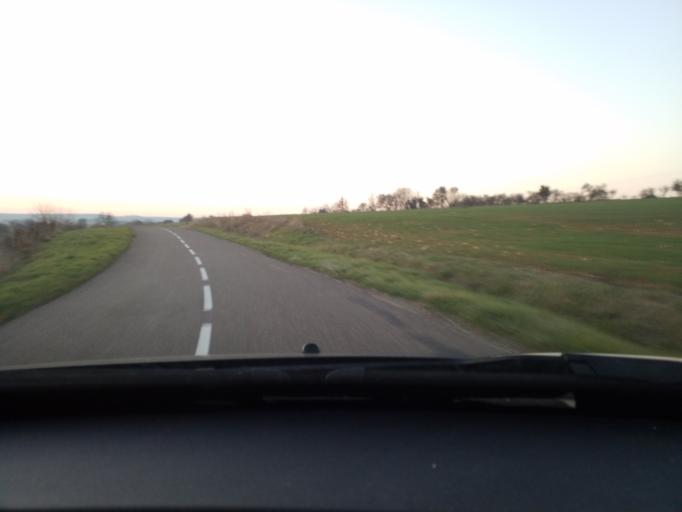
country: FR
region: Franche-Comte
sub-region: Departement de la Haute-Saone
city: Faverney
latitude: 47.8824
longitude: 6.1440
